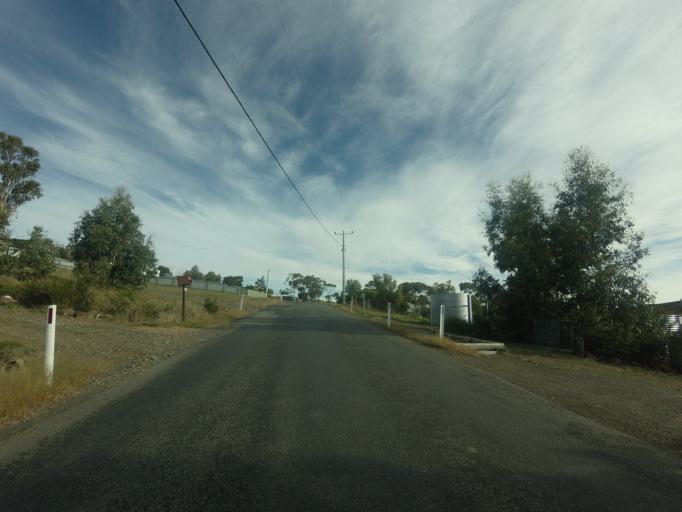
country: AU
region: Tasmania
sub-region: Sorell
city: Sorell
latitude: -42.9473
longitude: 147.8531
